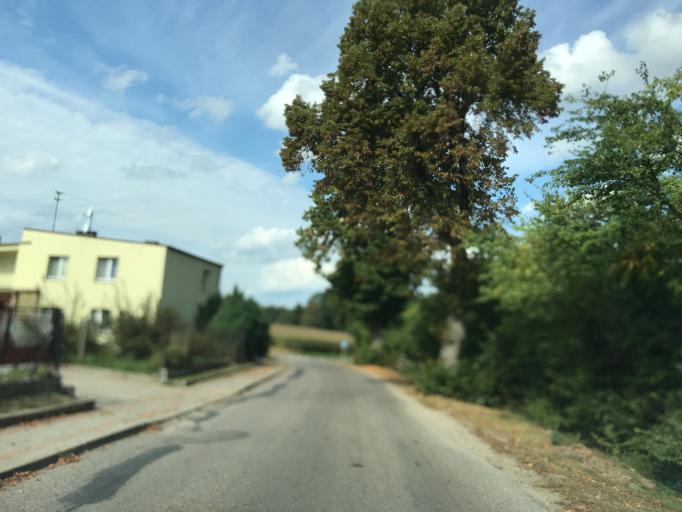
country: PL
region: Warmian-Masurian Voivodeship
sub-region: Powiat ilawski
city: Lubawa
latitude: 53.4101
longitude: 19.7539
